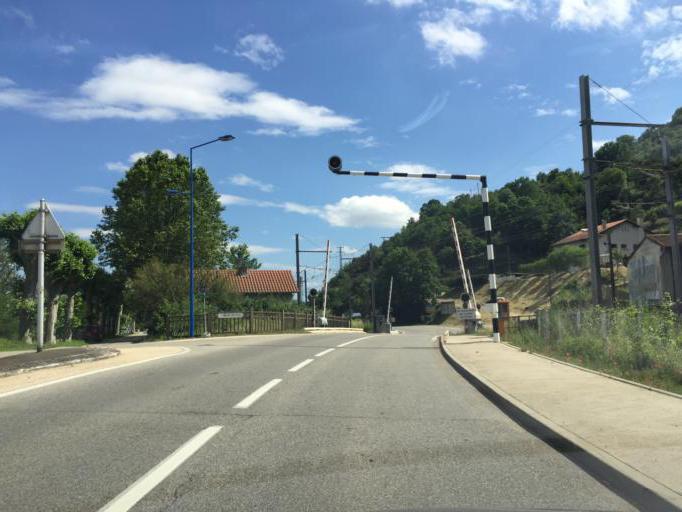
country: FR
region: Rhone-Alpes
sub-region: Departement de l'Ardeche
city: Andance
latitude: 45.2361
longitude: 4.7984
